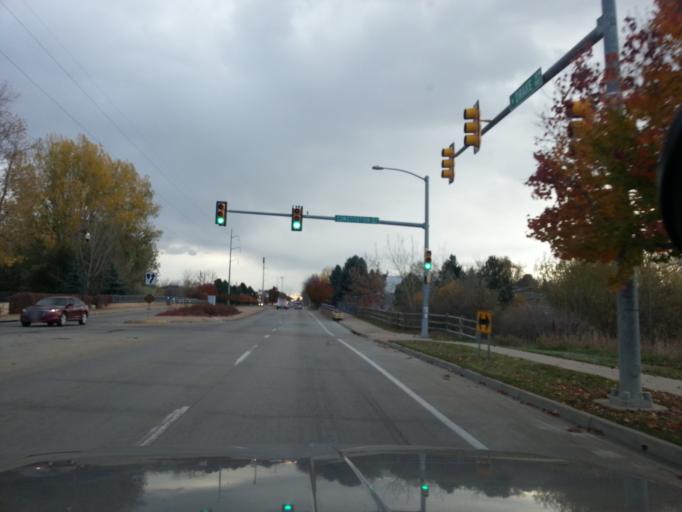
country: US
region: Colorado
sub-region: Larimer County
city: Fort Collins
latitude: 40.5527
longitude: -105.1089
